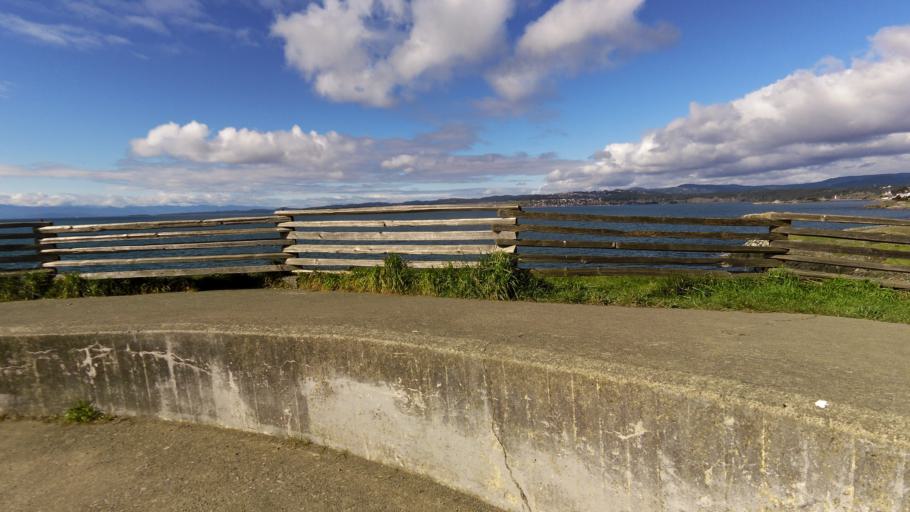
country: CA
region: British Columbia
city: Victoria
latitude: 48.4181
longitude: -123.4100
